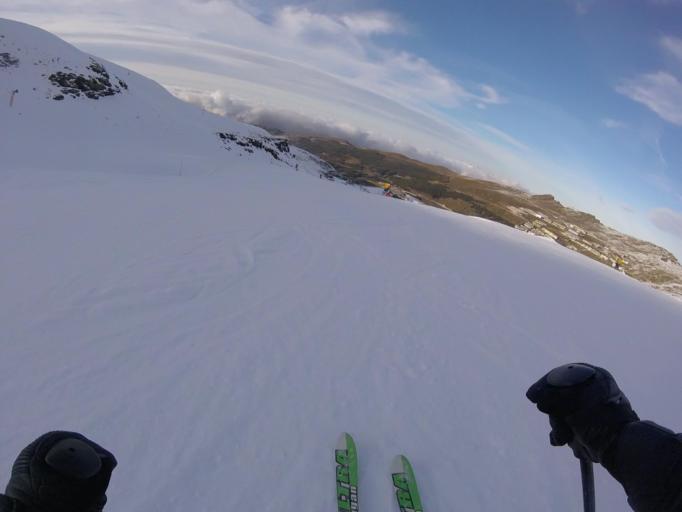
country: ES
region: Andalusia
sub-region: Provincia de Granada
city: Guejar-Sierra
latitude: 37.0782
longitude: -3.4046
